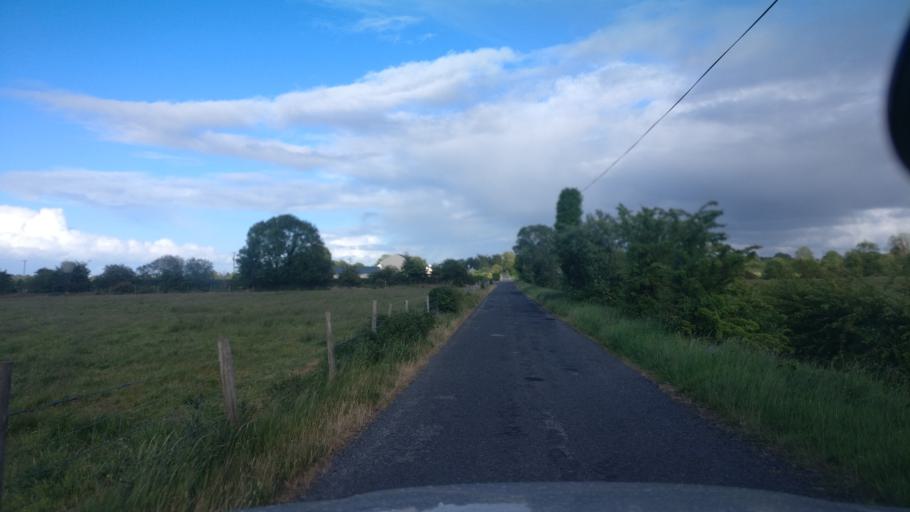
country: IE
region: Connaught
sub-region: County Galway
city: Ballinasloe
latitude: 53.2468
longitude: -8.2190
